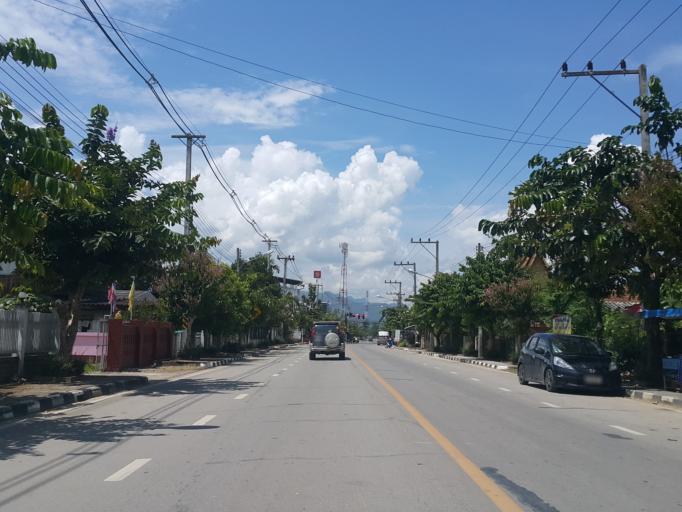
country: TH
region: Chiang Mai
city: Phrao
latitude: 19.3683
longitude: 99.2061
